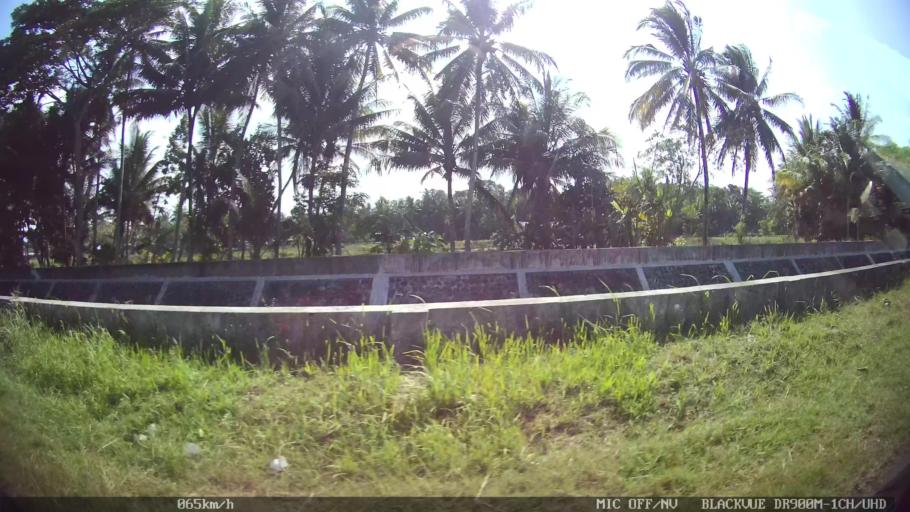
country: ID
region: Daerah Istimewa Yogyakarta
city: Srandakan
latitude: -7.9079
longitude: 110.1726
